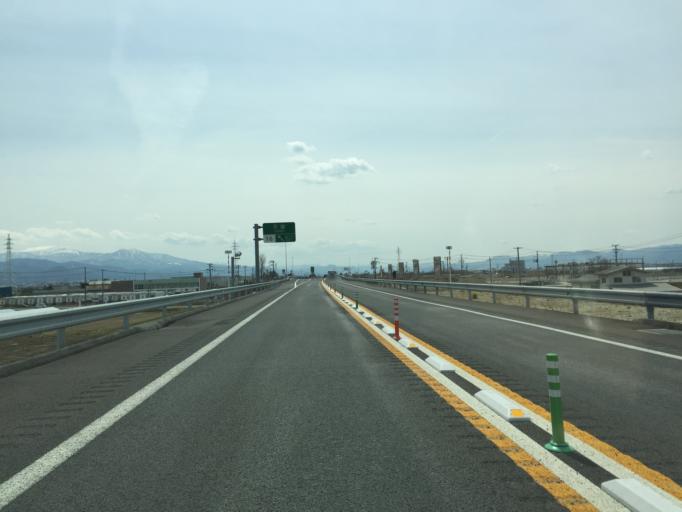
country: JP
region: Yamagata
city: Tendo
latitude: 38.3692
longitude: 140.3470
